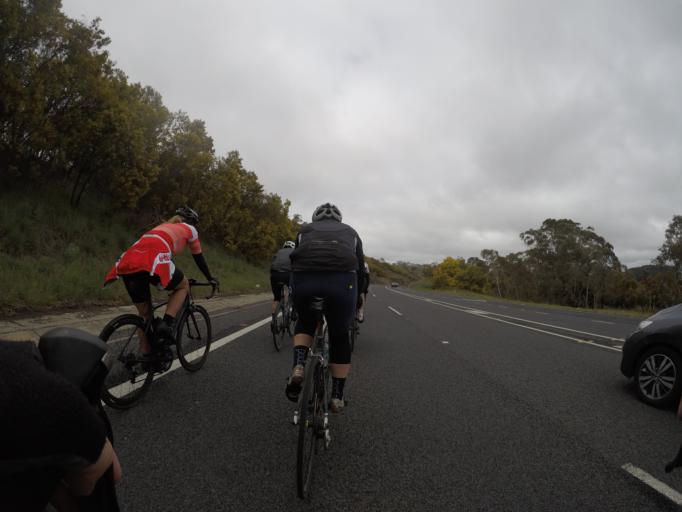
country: AU
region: New South Wales
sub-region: Lithgow
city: Portland
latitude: -33.4552
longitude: 149.9865
